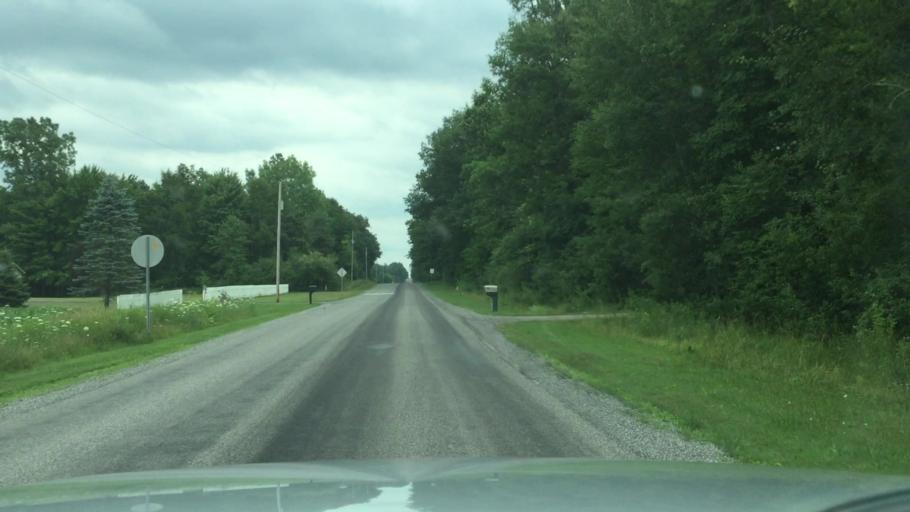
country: US
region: Michigan
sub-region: Saginaw County
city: Bridgeport
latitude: 43.3217
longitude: -83.8657
